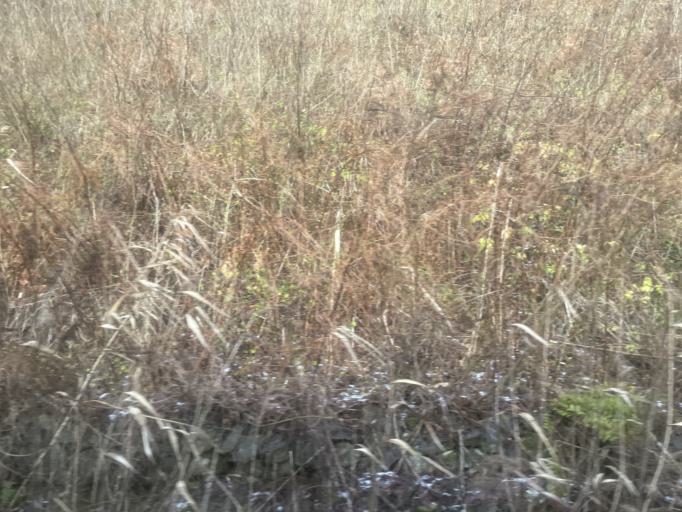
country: JP
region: Aomori
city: Goshogawara
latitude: 41.0768
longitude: 140.5411
